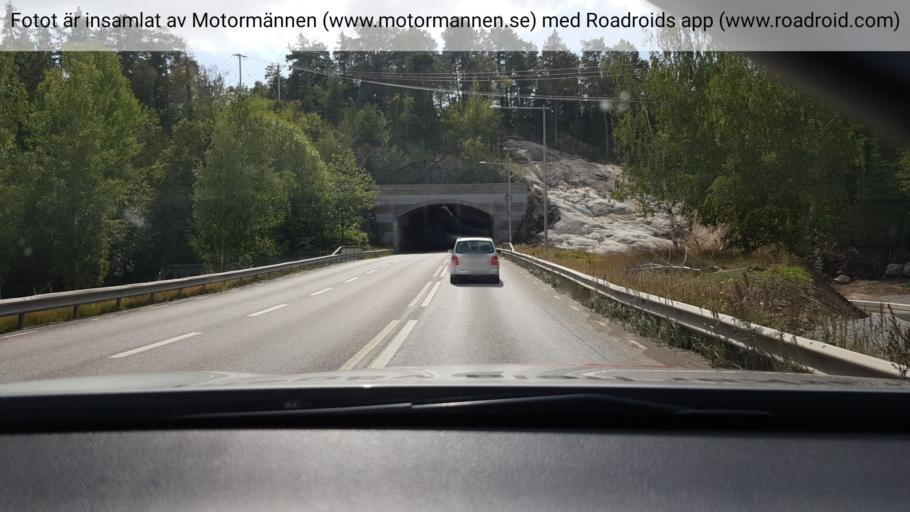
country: SE
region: Stockholm
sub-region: Ekero Kommun
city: Ekeroe
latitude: 59.3002
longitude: 17.8527
